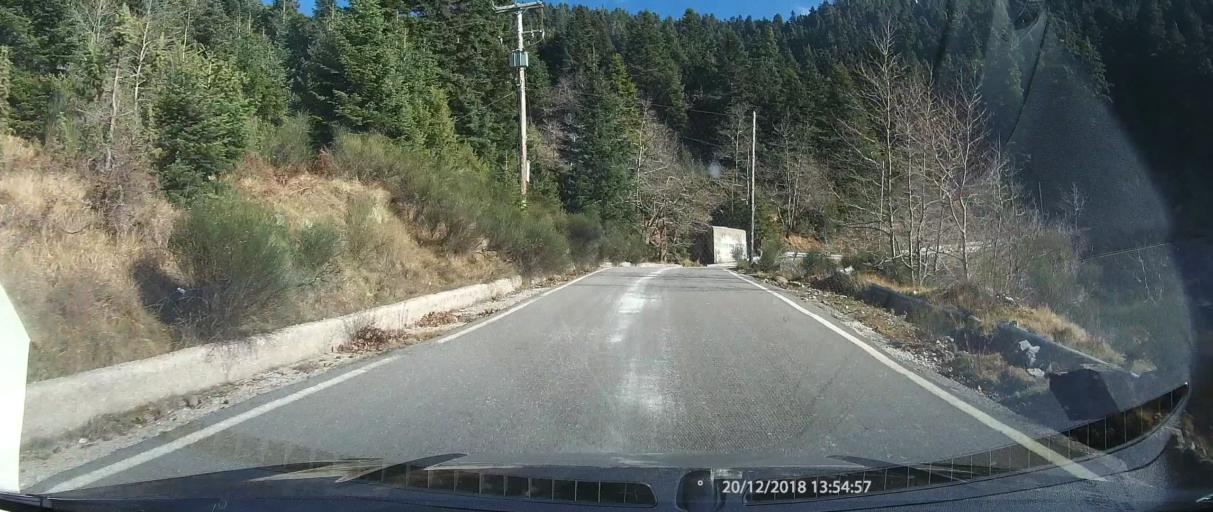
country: GR
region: West Greece
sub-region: Nomos Aitolias kai Akarnanias
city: Paravola
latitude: 38.7126
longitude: 21.6134
